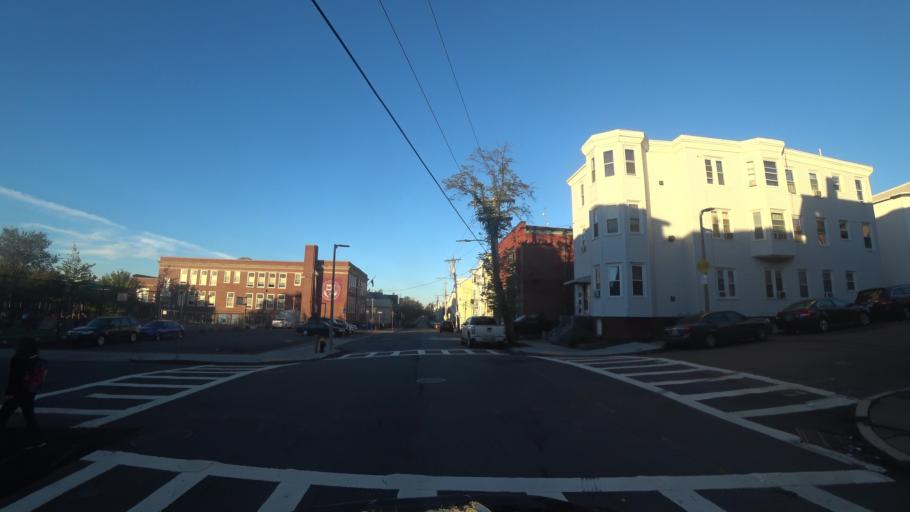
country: US
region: Massachusetts
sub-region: Suffolk County
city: Chelsea
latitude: 42.3791
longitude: -71.0297
